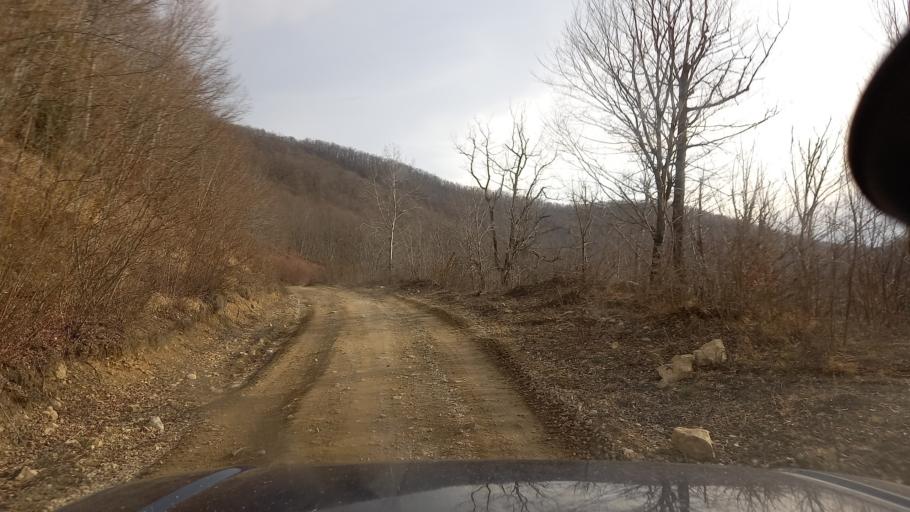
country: RU
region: Adygeya
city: Kamennomostskiy
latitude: 44.1483
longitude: 40.3025
